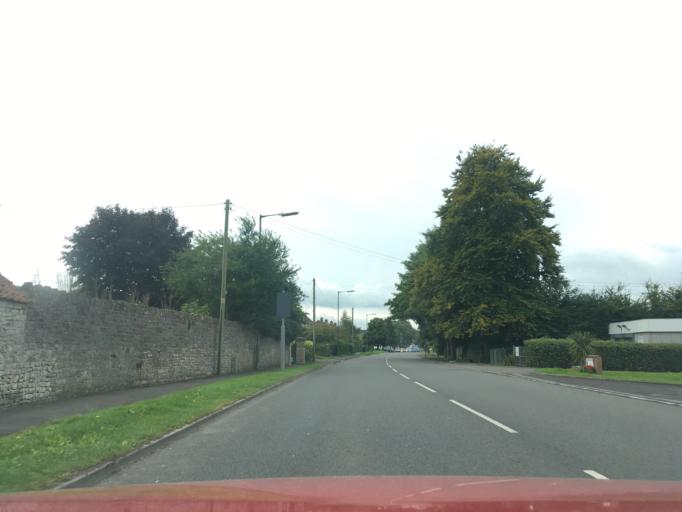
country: GB
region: England
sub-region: South Gloucestershire
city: Thornbury
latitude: 51.6150
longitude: -2.5178
